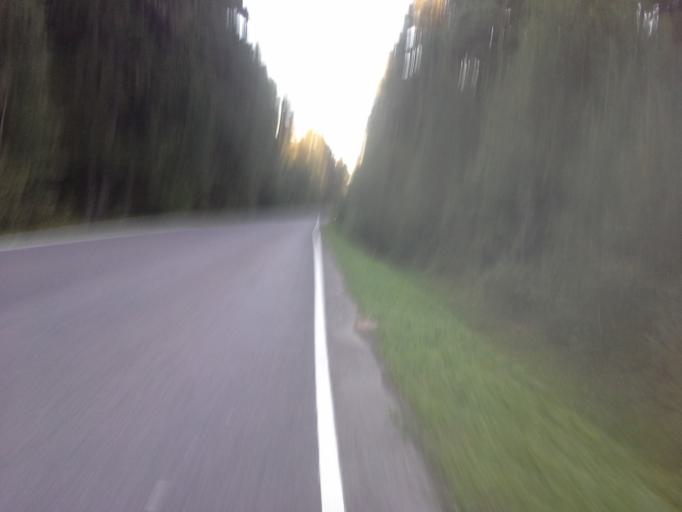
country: RU
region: Moskovskaya
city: Selyatino
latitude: 55.5123
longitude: 36.9383
